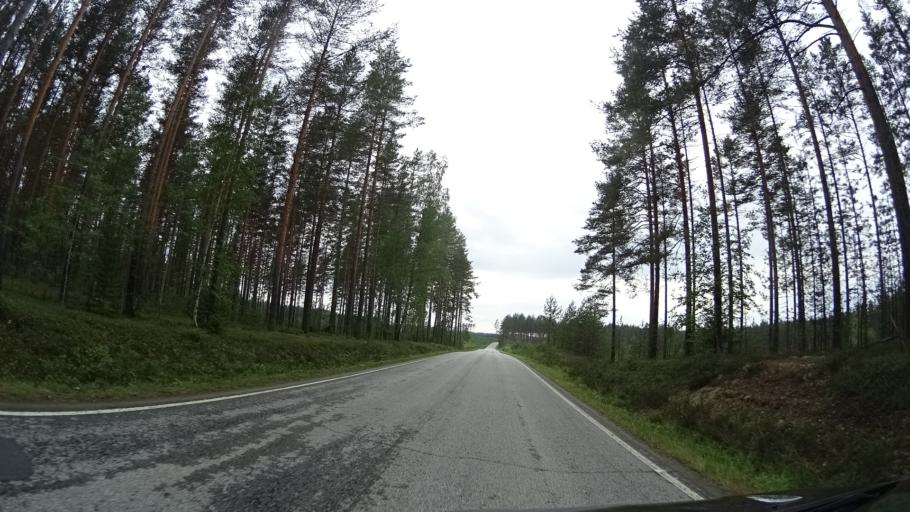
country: FI
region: Southern Savonia
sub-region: Savonlinna
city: Punkaharju
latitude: 61.7494
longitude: 29.4823
